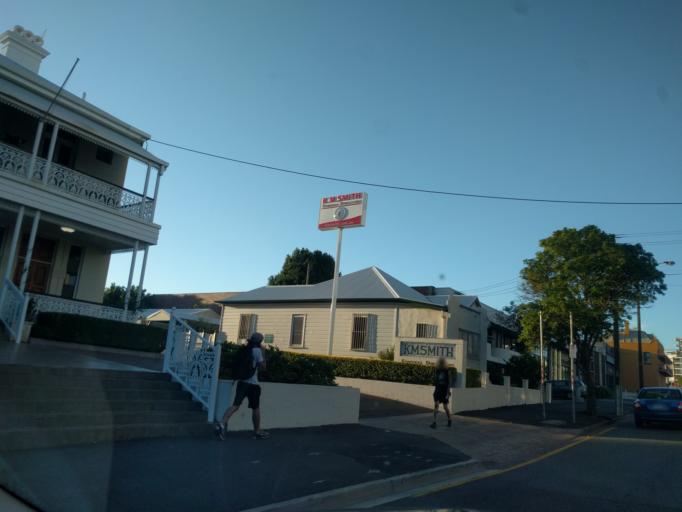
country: AU
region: Queensland
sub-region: Brisbane
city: Fortitude Valley
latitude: -27.4510
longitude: 153.0356
